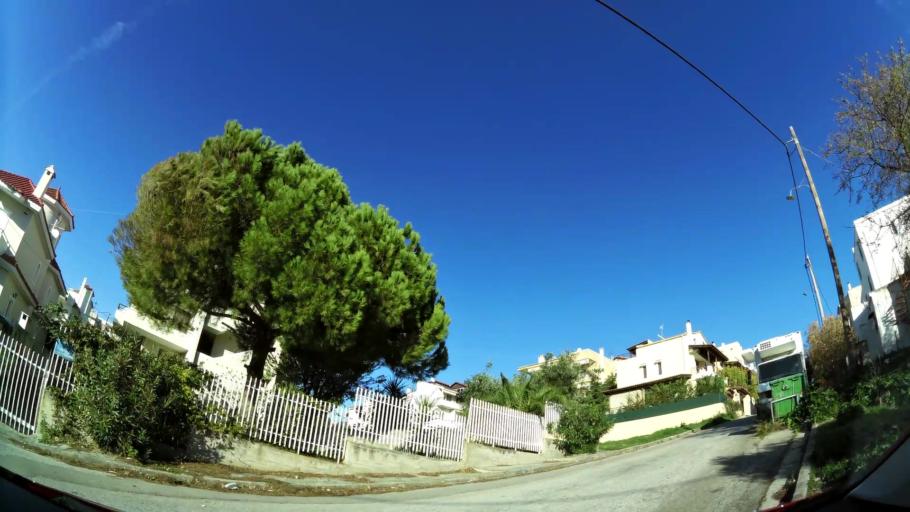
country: GR
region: Attica
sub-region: Nomarchia Anatolikis Attikis
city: Rafina
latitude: 38.0241
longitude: 23.9988
